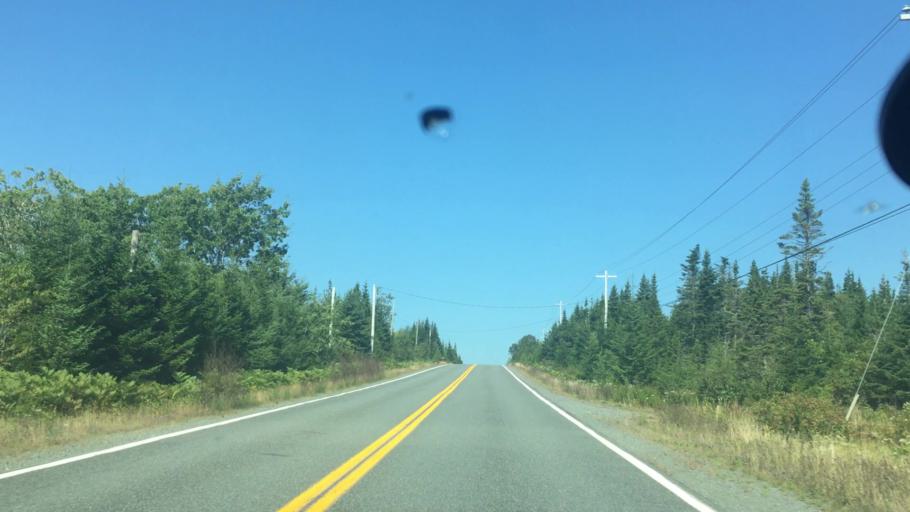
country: CA
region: Nova Scotia
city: Antigonish
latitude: 45.0027
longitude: -62.1015
